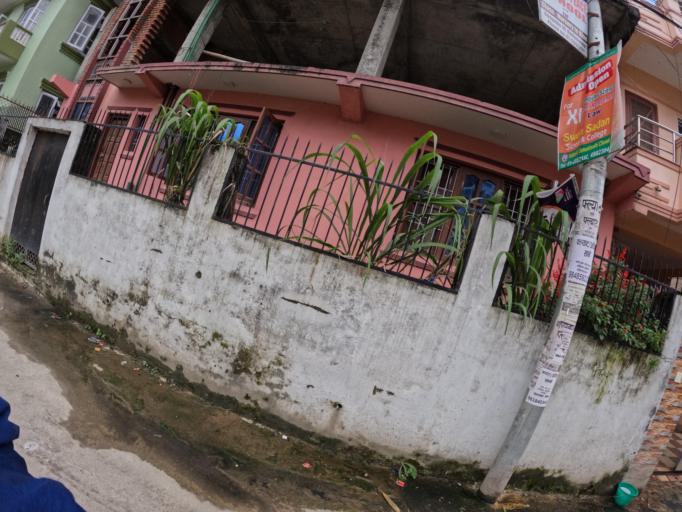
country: NP
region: Central Region
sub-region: Bagmati Zone
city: Kathmandu
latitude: 27.7360
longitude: 85.3168
